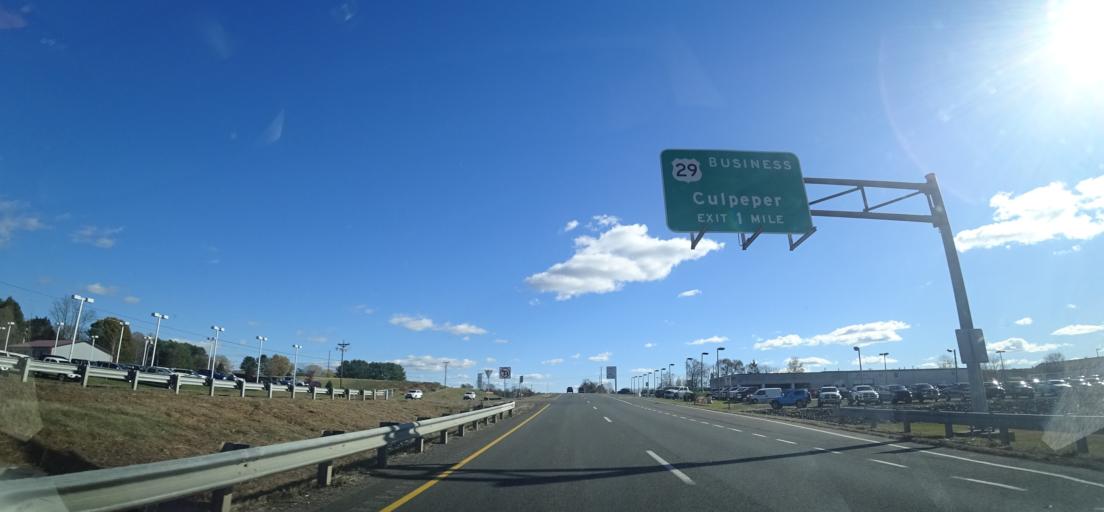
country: US
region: Virginia
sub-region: Culpeper County
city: Merrimac
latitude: 38.4574
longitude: -78.0480
